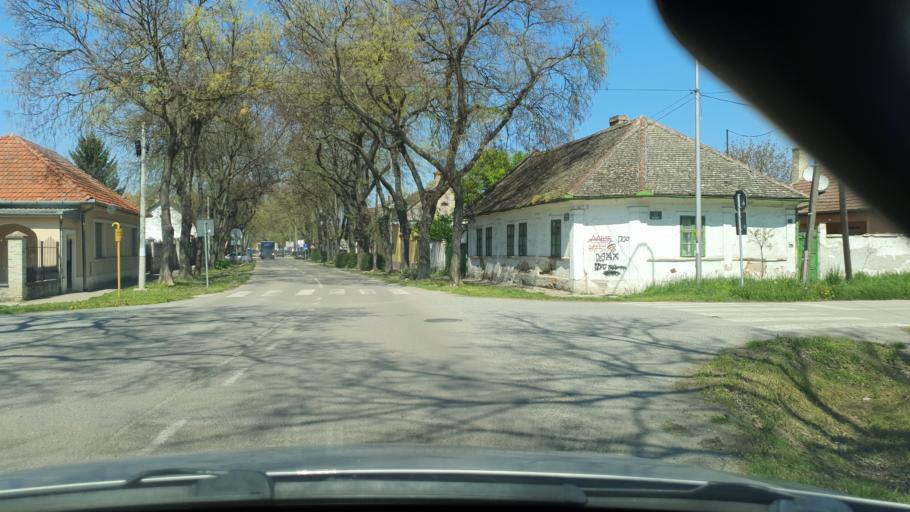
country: RS
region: Autonomna Pokrajina Vojvodina
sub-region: Zapadnobacki Okrug
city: Sombor
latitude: 45.7654
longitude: 19.1091
